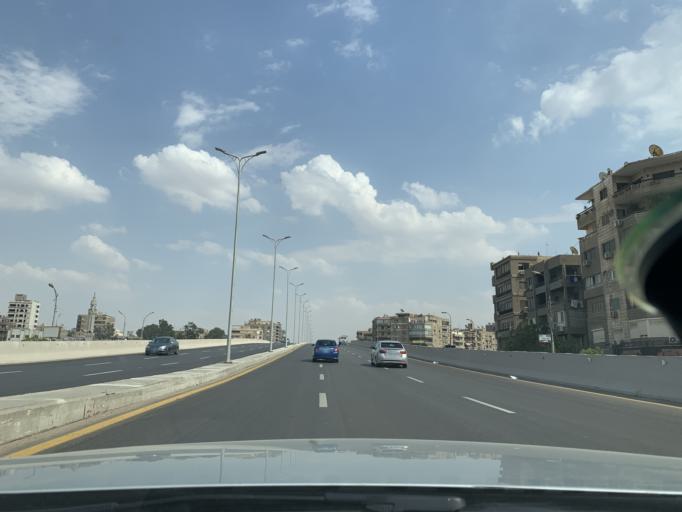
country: EG
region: Muhafazat al Qalyubiyah
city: Al Khankah
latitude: 30.1129
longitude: 31.3447
